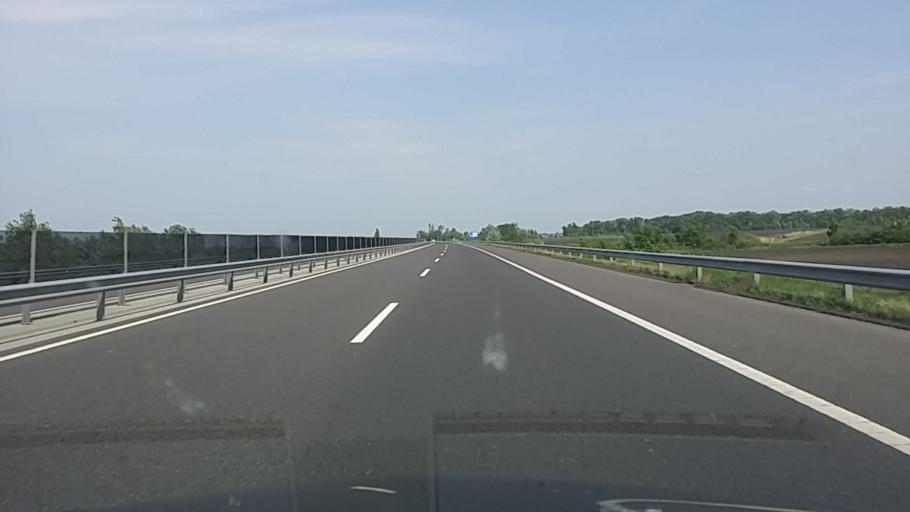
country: HU
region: Hajdu-Bihar
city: Gorbehaza
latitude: 47.8197
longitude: 21.3184
